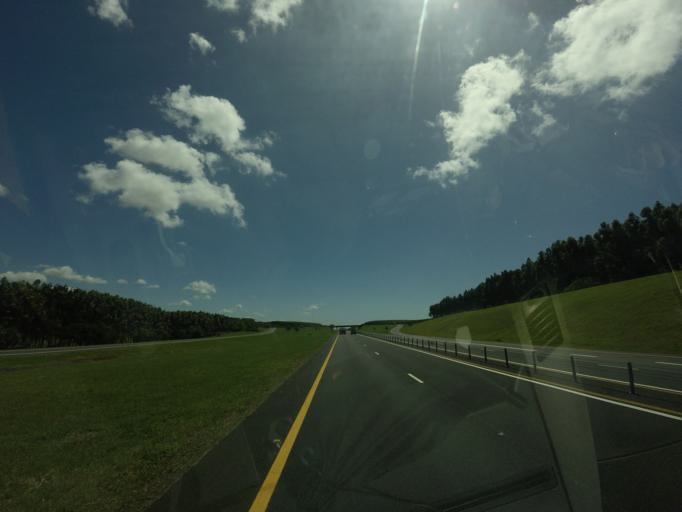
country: ZA
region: KwaZulu-Natal
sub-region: uThungulu District Municipality
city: Eshowe
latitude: -29.0436
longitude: 31.6459
